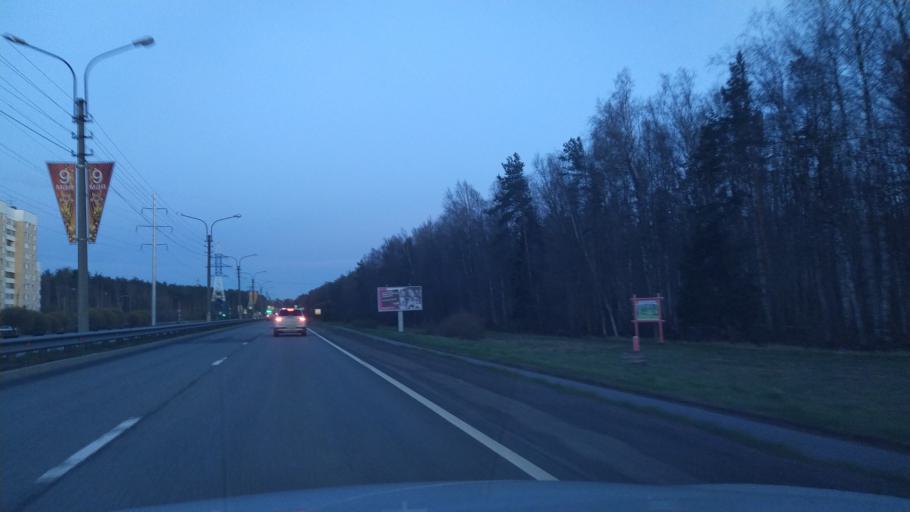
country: RU
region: St.-Petersburg
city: Razliv
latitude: 60.0782
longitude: 29.9622
